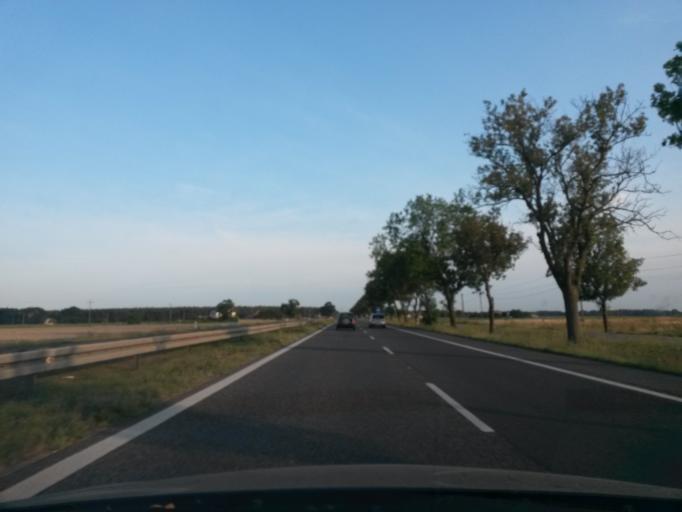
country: PL
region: Masovian Voivodeship
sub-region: Powiat nowodworski
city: Zakroczym
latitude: 52.4678
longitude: 20.5706
